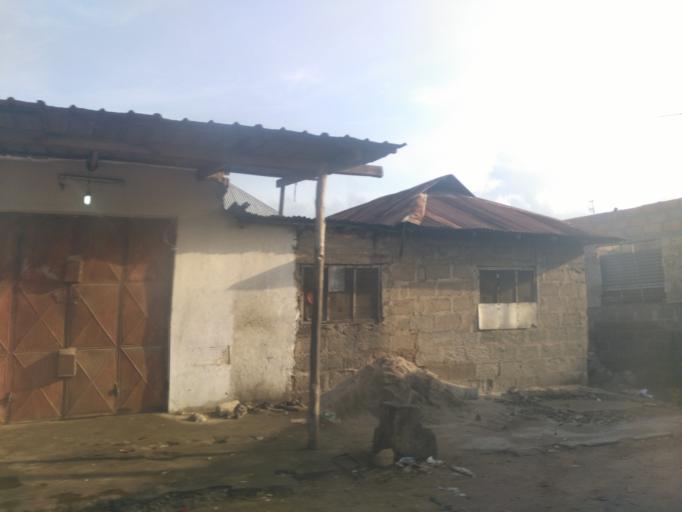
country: TZ
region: Zanzibar Urban/West
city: Zanzibar
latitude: -6.1773
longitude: 39.2139
